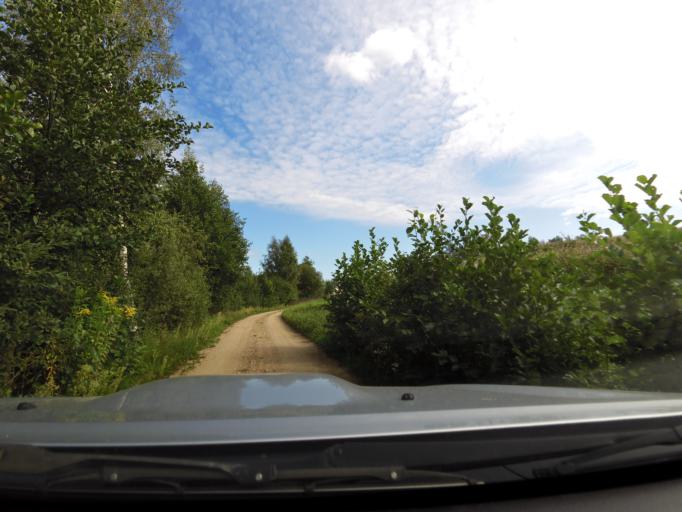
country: LT
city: Grigiskes
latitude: 54.7750
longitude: 25.0128
